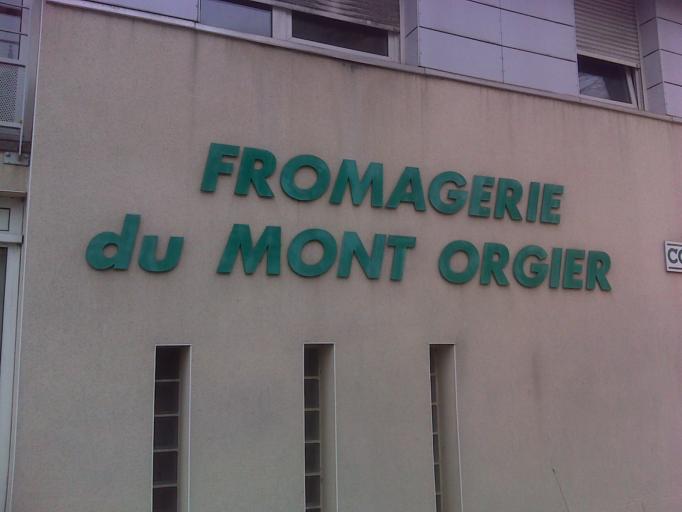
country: FR
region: Franche-Comte
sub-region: Departement du Jura
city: Orgelet
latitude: 46.5213
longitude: 5.6105
